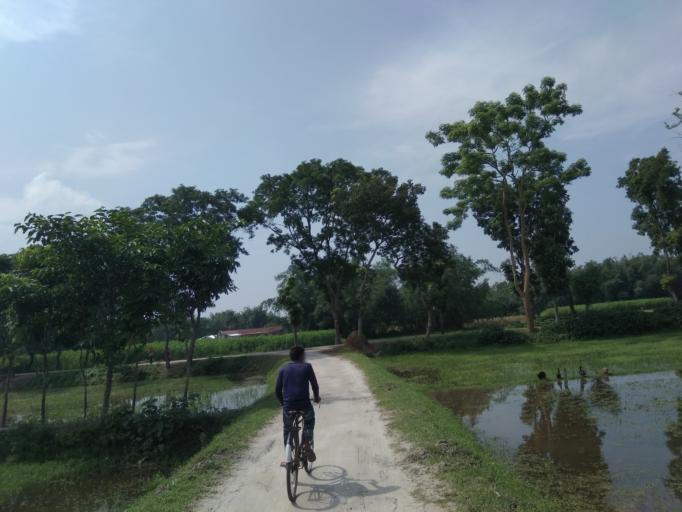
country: BD
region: Rangpur Division
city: Rangpur
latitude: 25.8380
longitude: 89.2045
